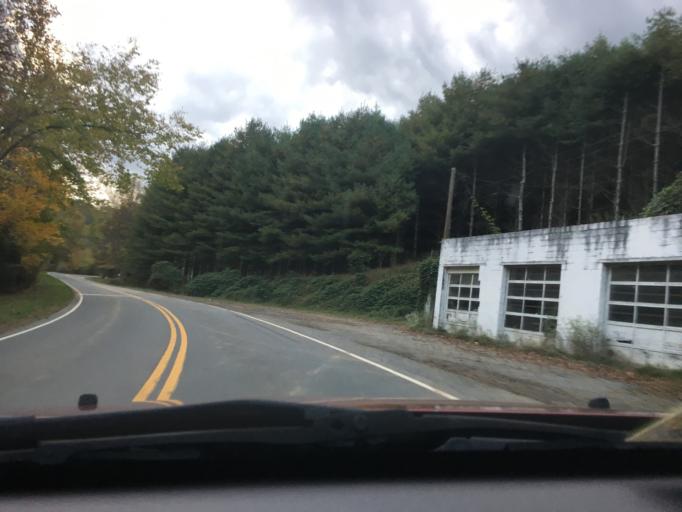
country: US
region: Virginia
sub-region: Giles County
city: Pearisburg
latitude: 37.2137
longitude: -80.7804
